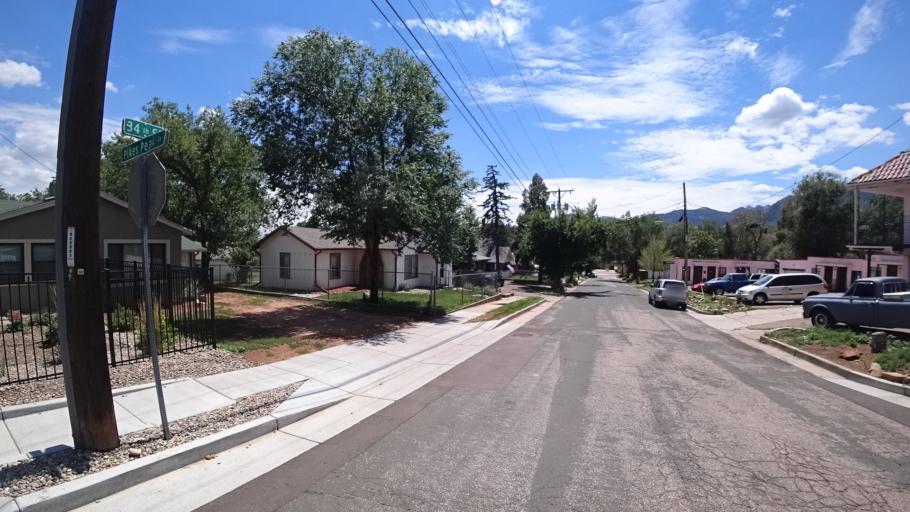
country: US
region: Colorado
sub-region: El Paso County
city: Manitou Springs
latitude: 38.8572
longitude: -104.8781
